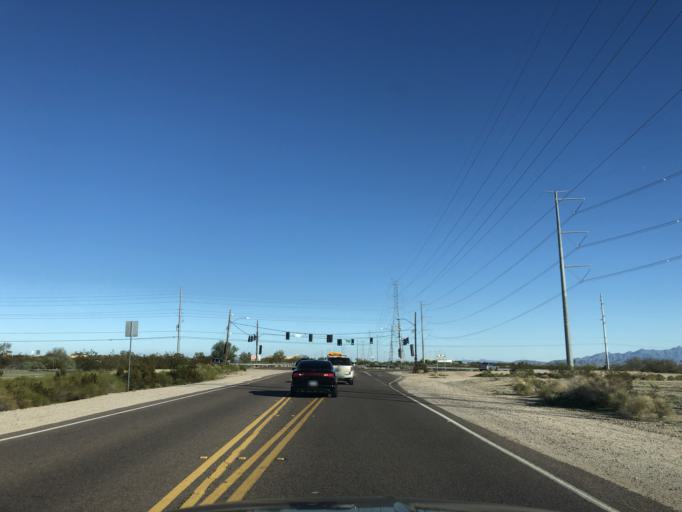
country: US
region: Arizona
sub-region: Maricopa County
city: Buckeye
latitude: 33.4209
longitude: -112.5922
